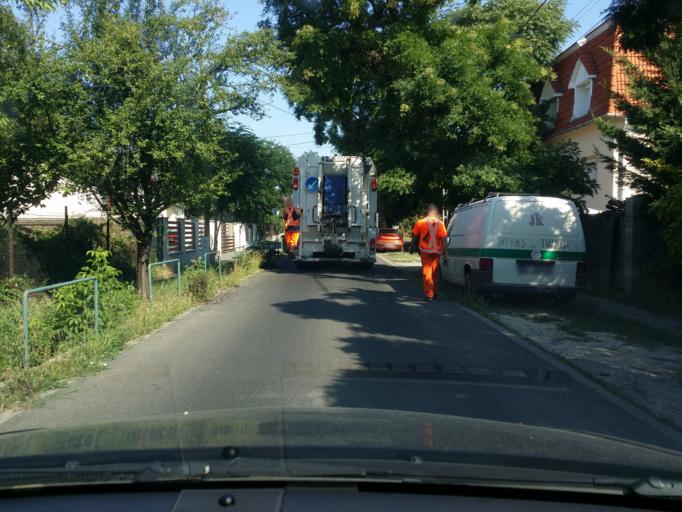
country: HU
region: Budapest
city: Budapest XVI. keruelet
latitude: 47.5283
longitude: 19.1602
